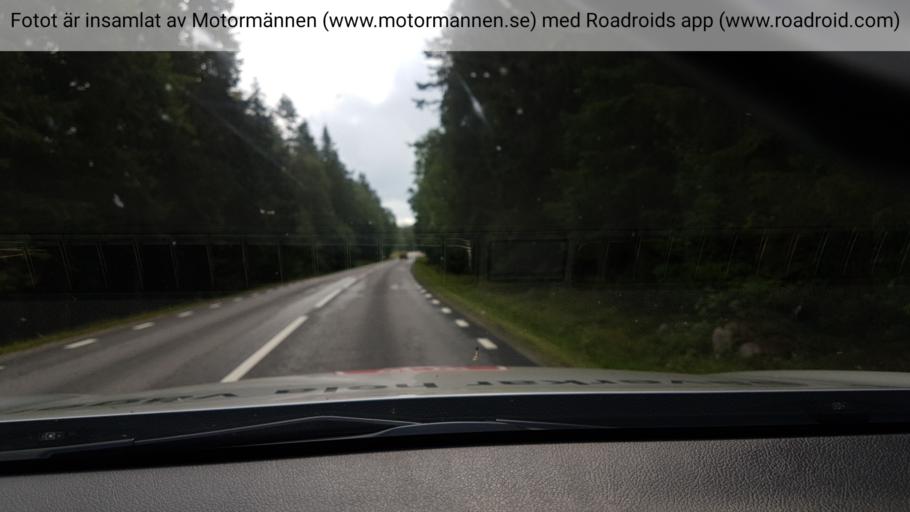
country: SE
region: Vaestra Goetaland
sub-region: Svenljunga Kommun
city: Svenljunga
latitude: 57.4799
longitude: 13.1571
